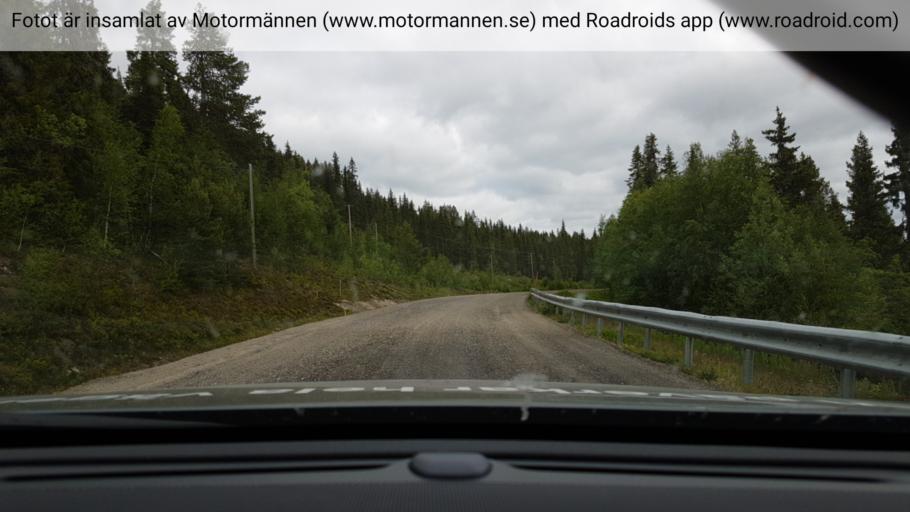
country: SE
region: Vaesterbotten
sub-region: Storumans Kommun
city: Fristad
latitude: 65.8184
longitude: 16.7943
